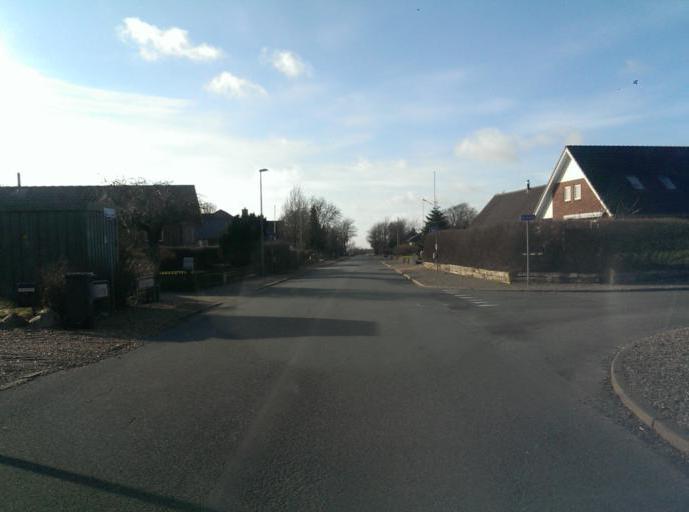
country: DK
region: South Denmark
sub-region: Esbjerg Kommune
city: Bramming
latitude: 55.4311
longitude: 8.6422
